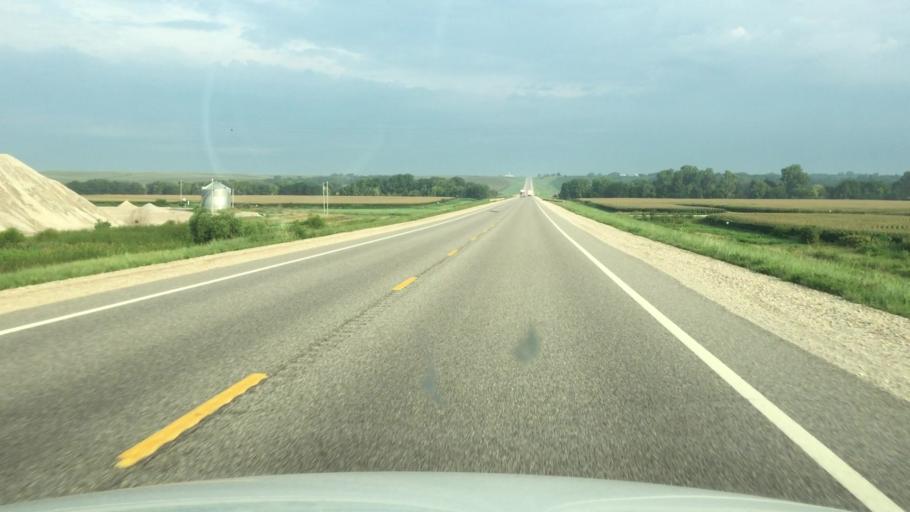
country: US
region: Kansas
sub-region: Doniphan County
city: Highland
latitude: 39.8118
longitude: -95.1959
